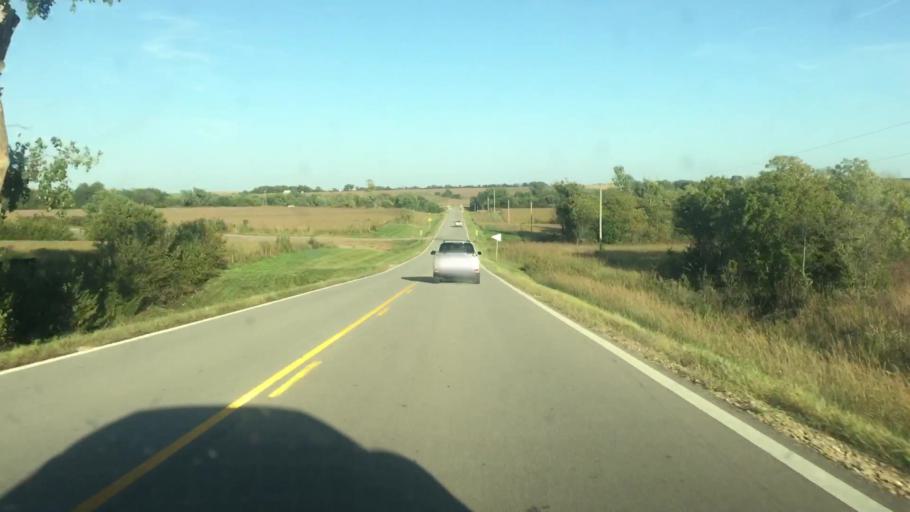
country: US
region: Kansas
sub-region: Brown County
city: Horton
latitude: 39.5875
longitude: -95.5420
